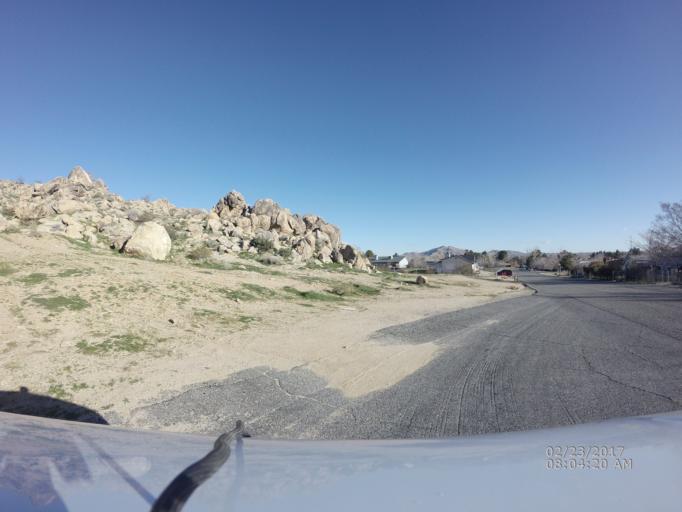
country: US
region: California
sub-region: Los Angeles County
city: Lake Los Angeles
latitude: 34.6104
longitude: -117.8201
